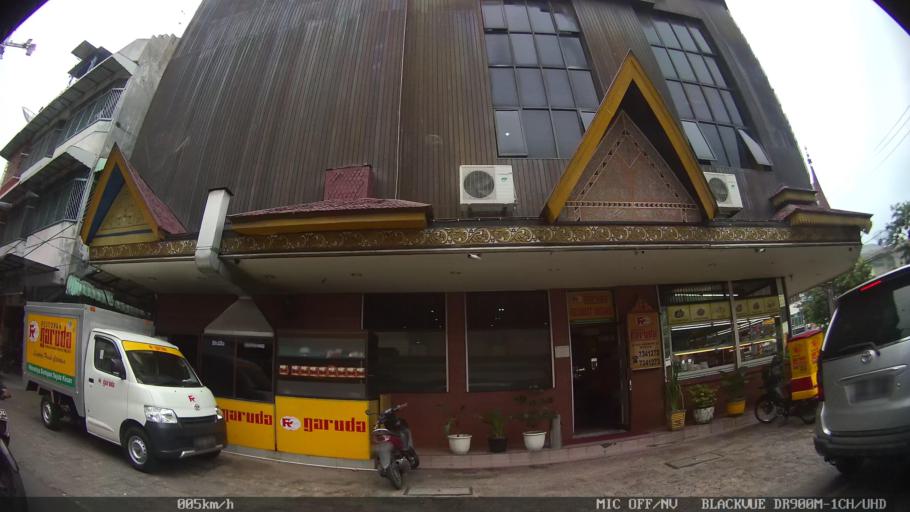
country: ID
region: North Sumatra
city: Medan
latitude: 3.5856
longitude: 98.7048
